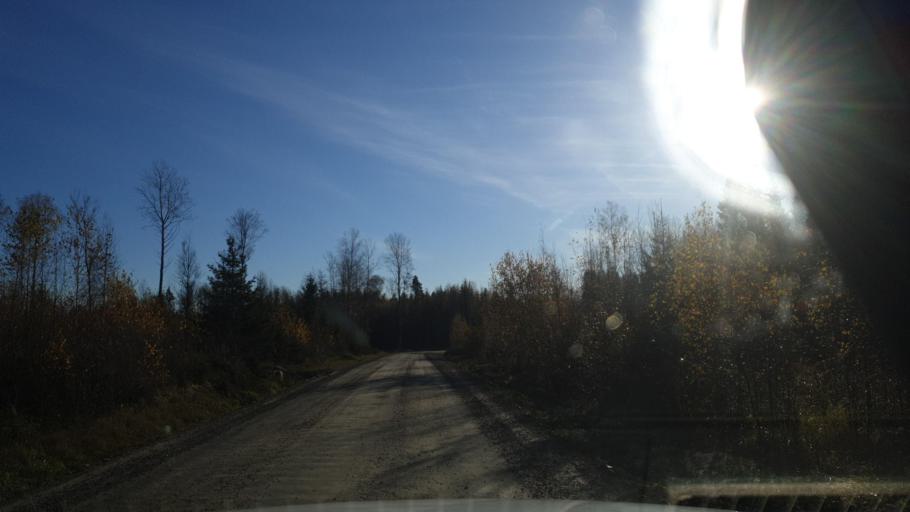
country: SE
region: Vaermland
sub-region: Karlstads Kommun
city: Edsvalla
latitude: 59.4829
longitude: 13.0713
